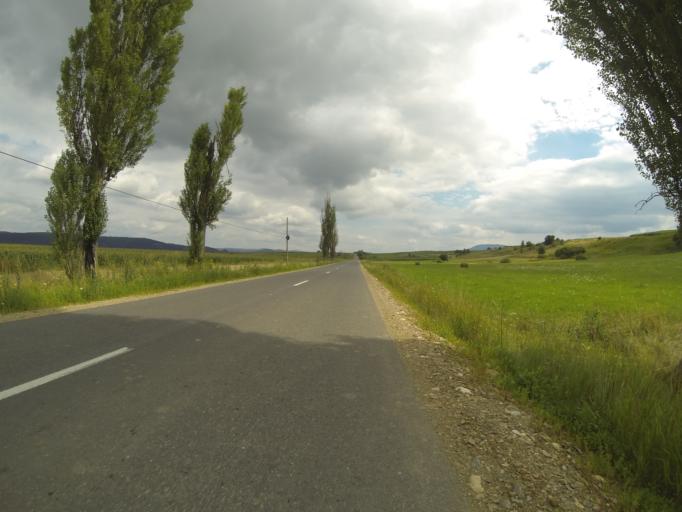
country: RO
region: Brasov
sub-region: Comuna Parau
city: Parau
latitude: 45.8623
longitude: 25.1995
